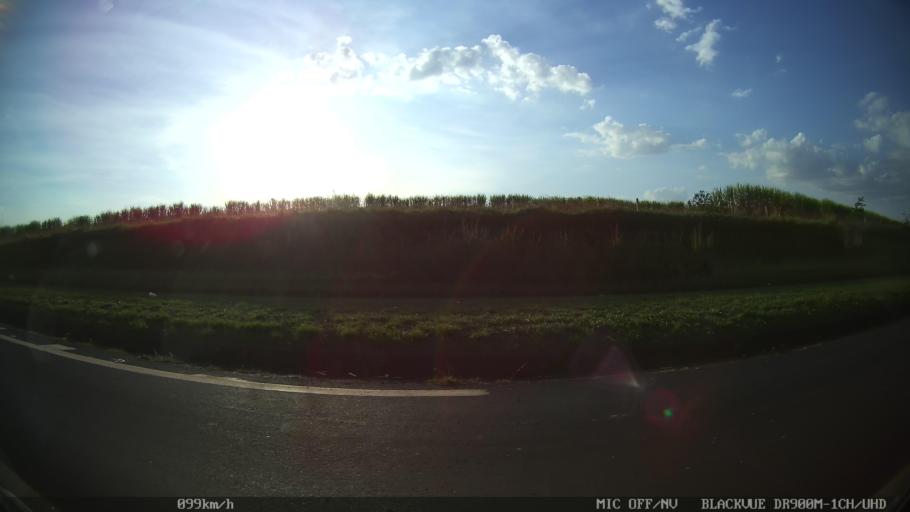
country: BR
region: Sao Paulo
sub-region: Ribeirao Preto
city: Ribeirao Preto
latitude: -21.1085
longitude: -47.7719
